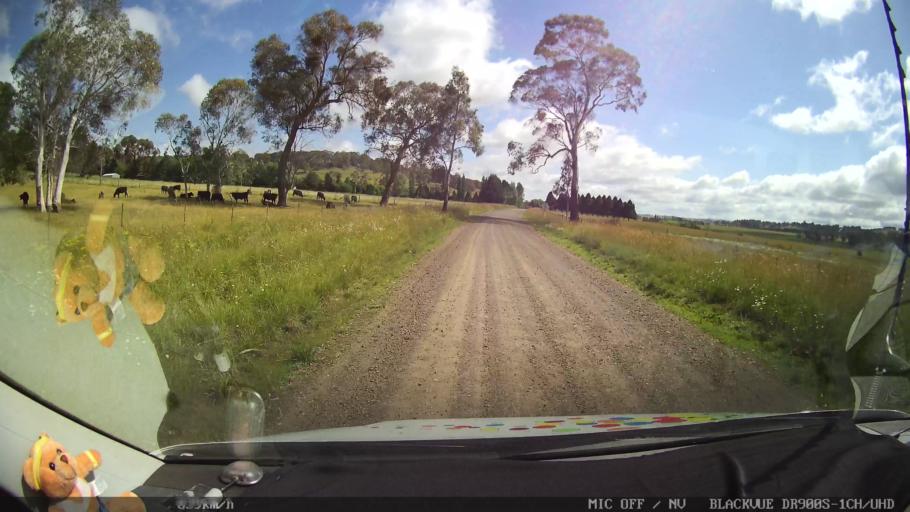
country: AU
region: New South Wales
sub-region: Glen Innes Severn
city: Glen Innes
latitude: -29.9623
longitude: 151.7000
